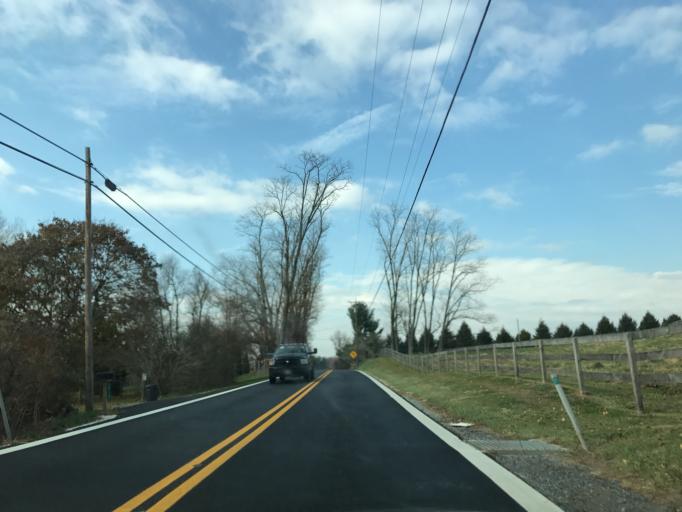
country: US
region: Maryland
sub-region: Baltimore County
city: Hunt Valley
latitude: 39.5856
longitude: -76.5902
